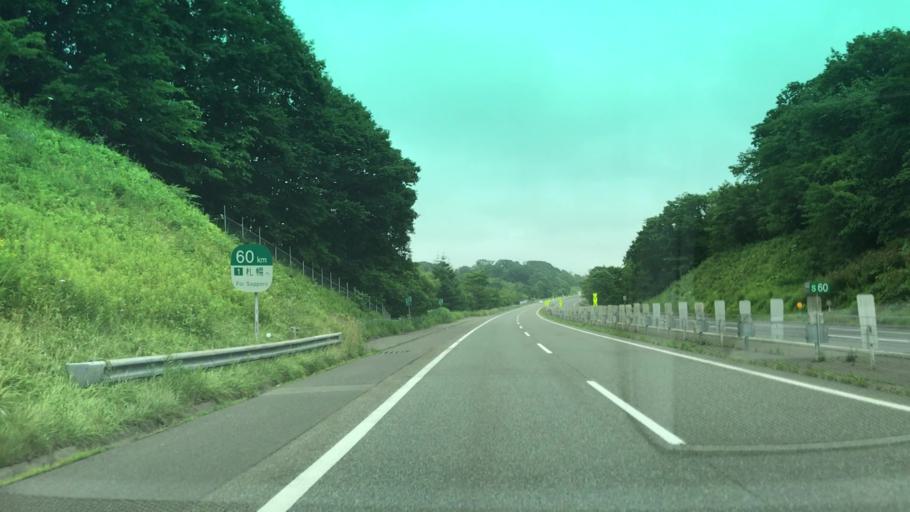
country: JP
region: Hokkaido
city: Tomakomai
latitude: 42.6505
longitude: 141.5438
